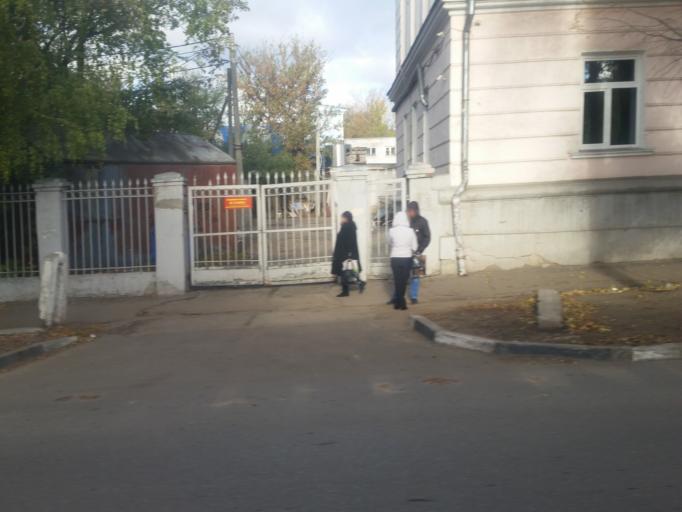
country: RU
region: Ulyanovsk
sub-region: Ulyanovskiy Rayon
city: Ulyanovsk
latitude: 54.3234
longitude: 48.3935
